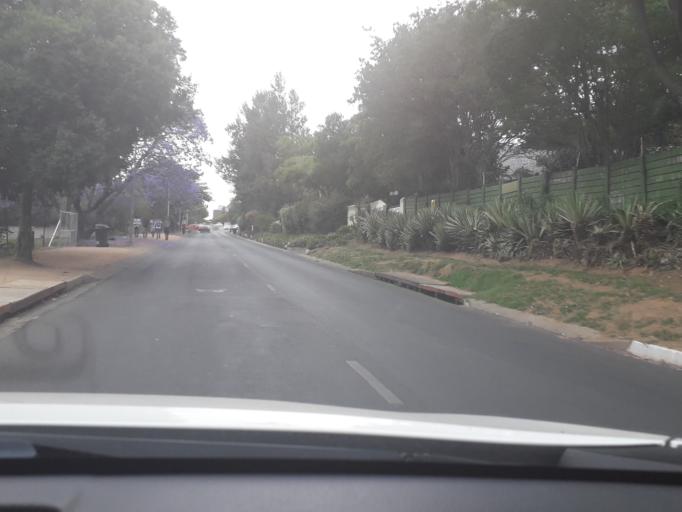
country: ZA
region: Gauteng
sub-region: City of Johannesburg Metropolitan Municipality
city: Johannesburg
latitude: -26.0884
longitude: 27.9956
